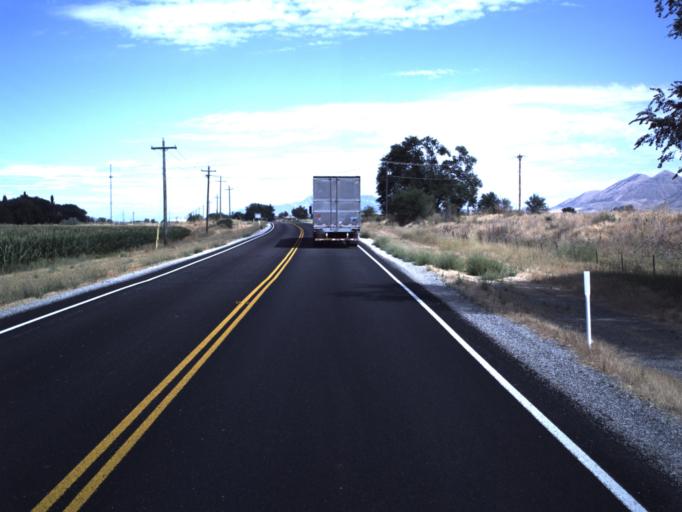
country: US
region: Utah
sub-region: Box Elder County
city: Honeyville
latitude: 41.6262
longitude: -112.1268
